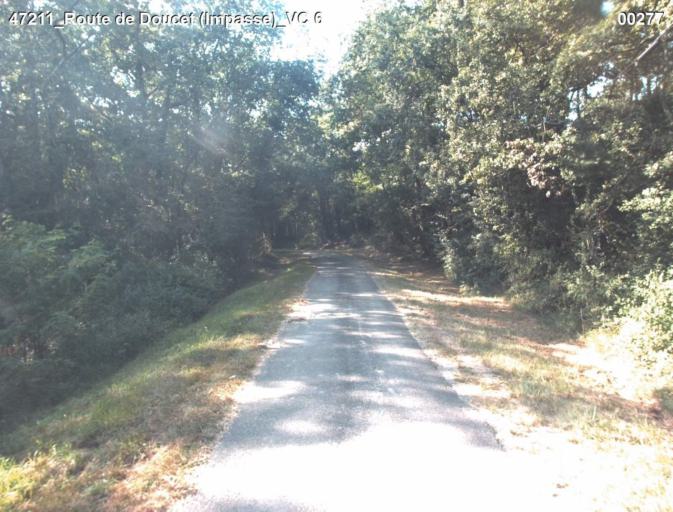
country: FR
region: Aquitaine
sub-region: Departement du Lot-et-Garonne
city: Mezin
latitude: 44.0201
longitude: 0.1999
